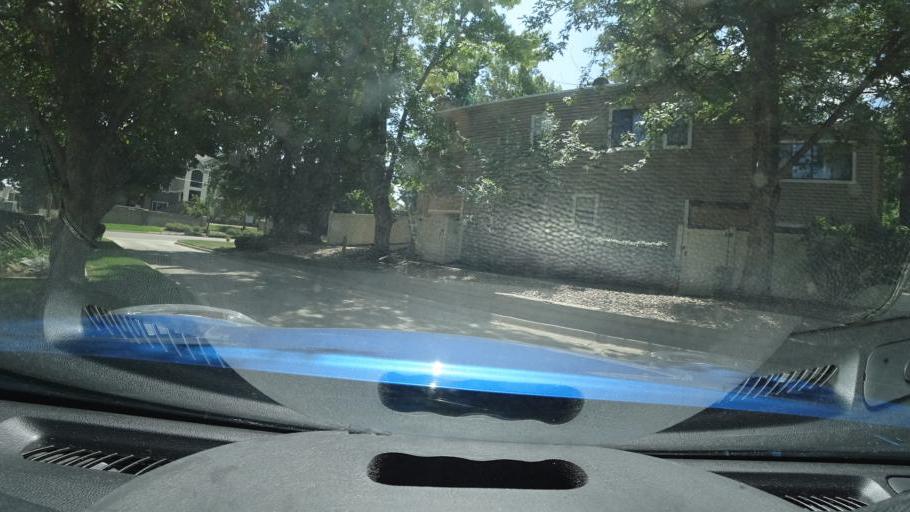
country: US
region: Colorado
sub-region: Adams County
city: Aurora
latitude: 39.6954
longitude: -104.8759
